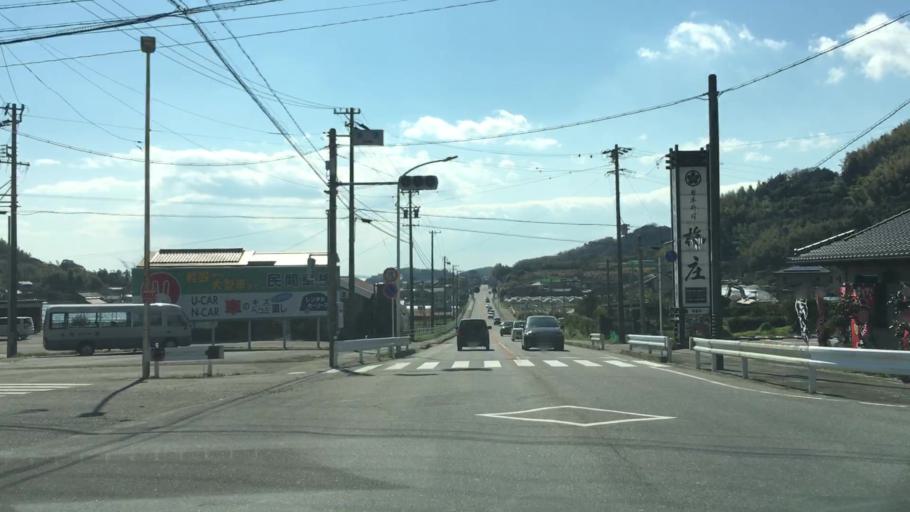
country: JP
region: Aichi
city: Gamagori
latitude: 34.7967
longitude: 137.1592
